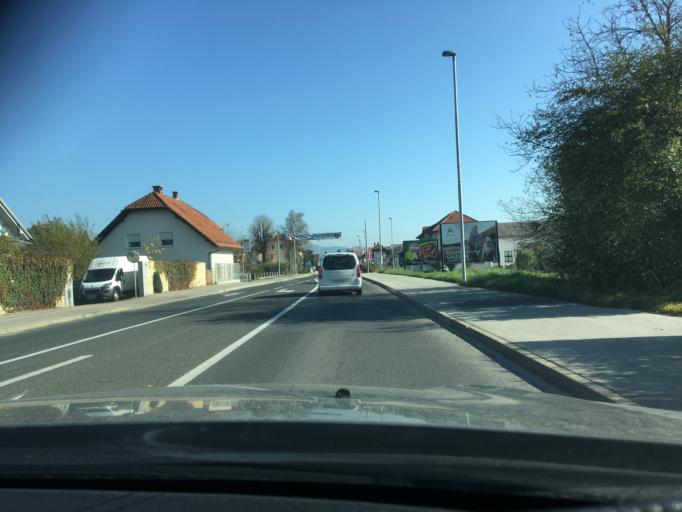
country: SI
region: Domzale
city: Vir
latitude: 46.1477
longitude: 14.6077
